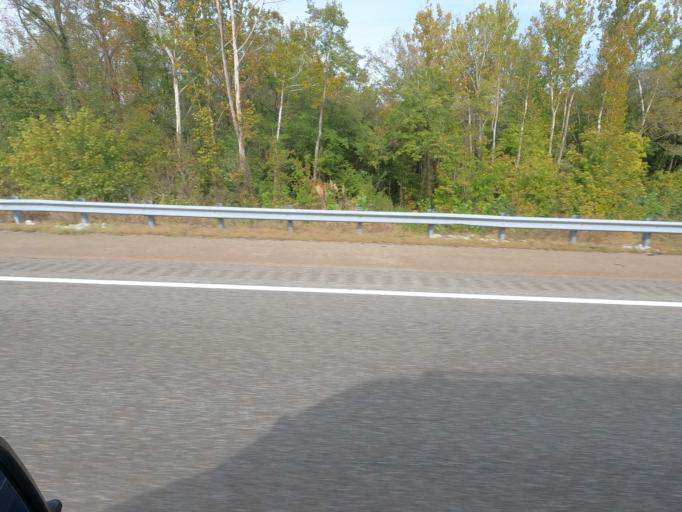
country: US
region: Tennessee
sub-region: Henderson County
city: Lexington
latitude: 35.8013
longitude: -88.3429
